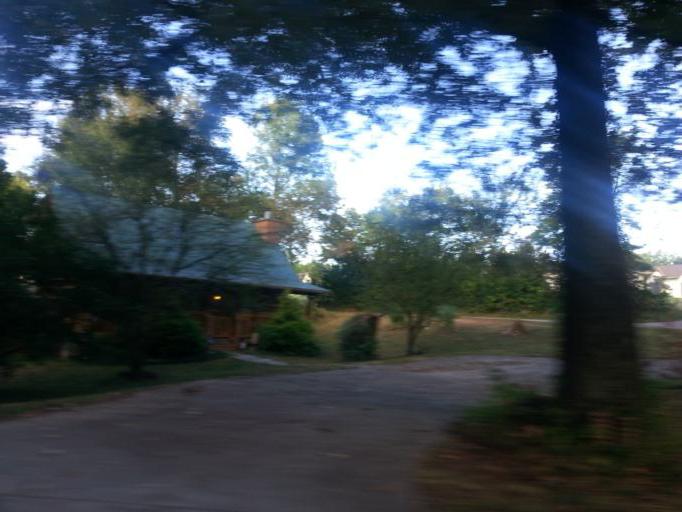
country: US
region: Tennessee
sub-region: Blount County
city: Eagleton Village
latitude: 35.8215
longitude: -83.9449
